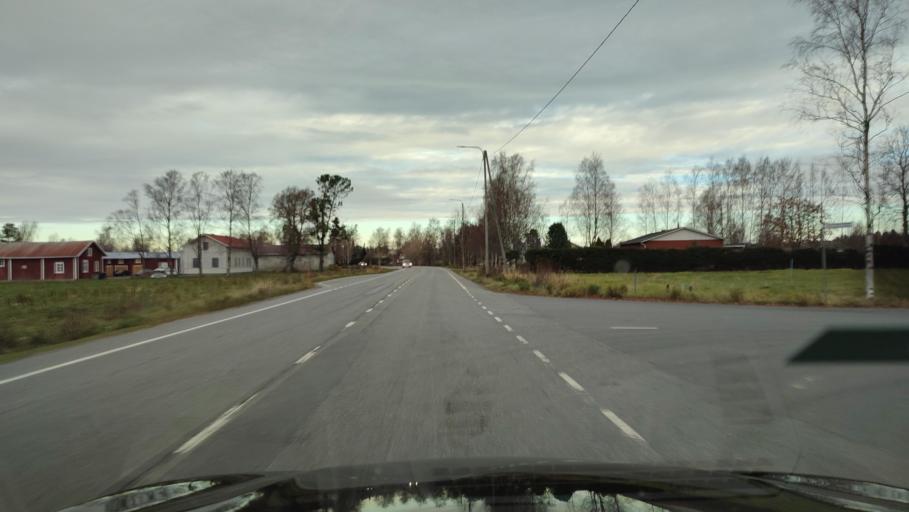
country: FI
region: Ostrobothnia
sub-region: Sydosterbotten
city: Naerpes
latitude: 62.4602
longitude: 21.3559
